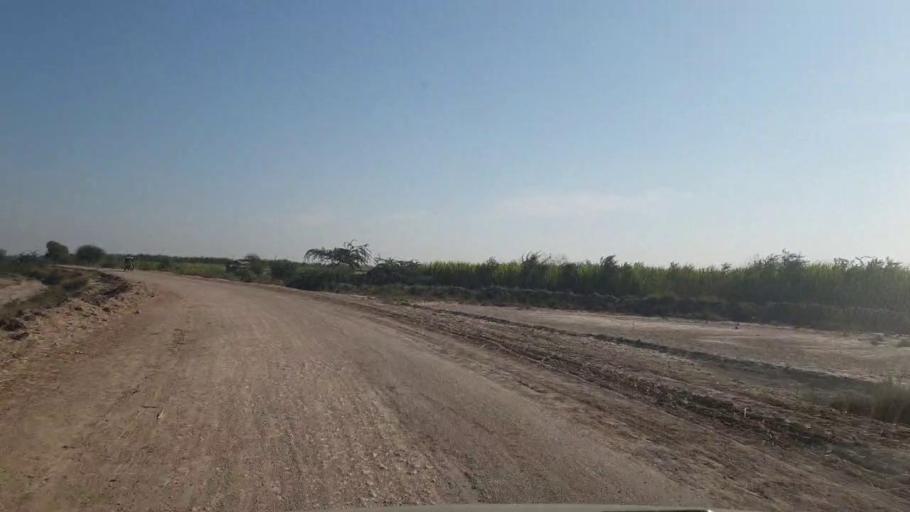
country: PK
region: Sindh
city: Rajo Khanani
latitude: 24.9715
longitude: 68.7746
